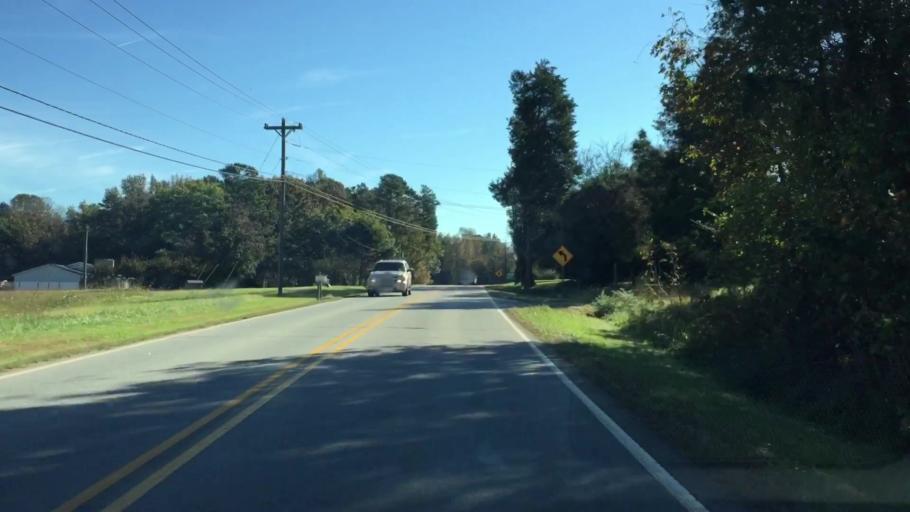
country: US
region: North Carolina
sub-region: Rowan County
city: China Grove
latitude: 35.6506
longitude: -80.6040
